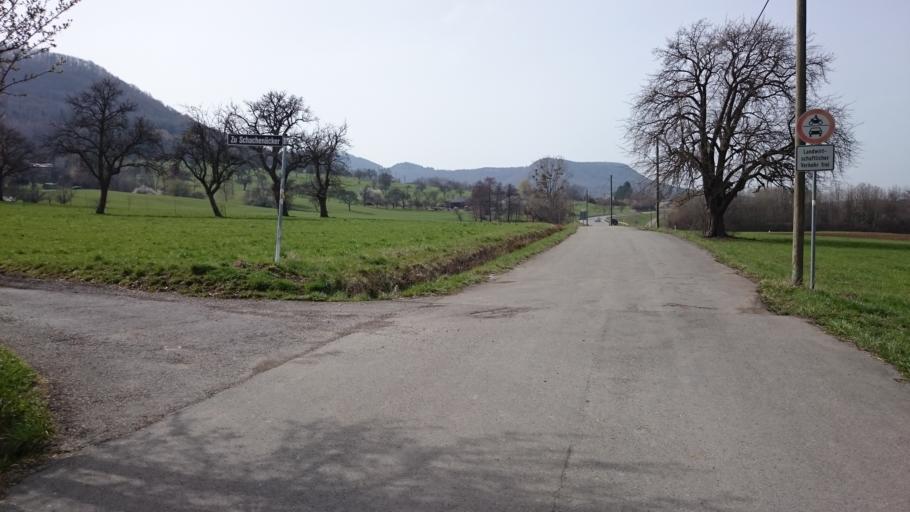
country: DE
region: Baden-Wuerttemberg
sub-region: Tuebingen Region
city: Gomaringen
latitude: 48.4471
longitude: 9.1551
